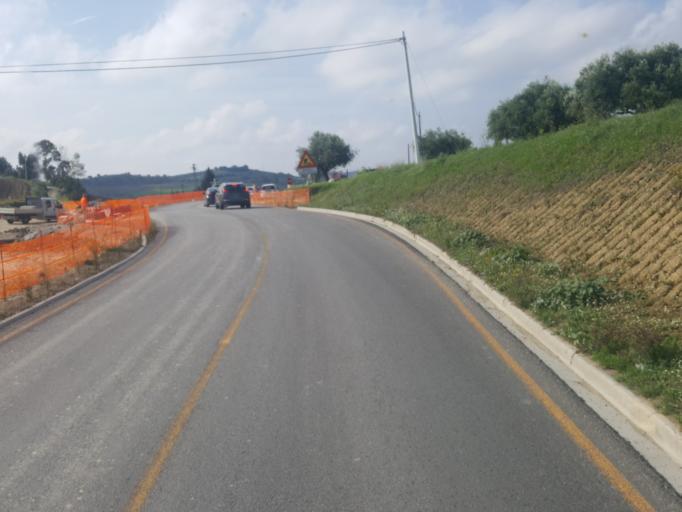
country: IT
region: Sicily
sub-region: Provincia di Caltanissetta
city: San Cataldo
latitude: 37.4478
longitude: 13.9578
